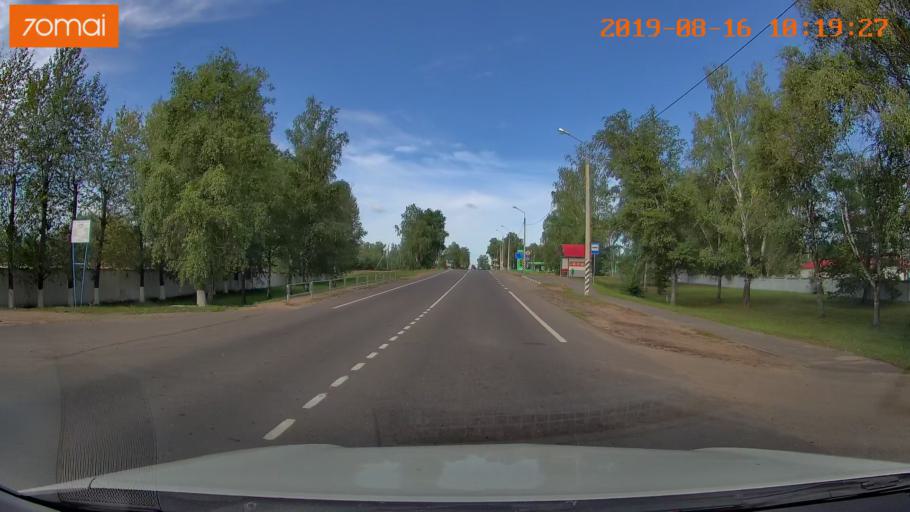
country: BY
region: Mogilev
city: Asipovichy
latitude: 53.3063
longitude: 28.6664
